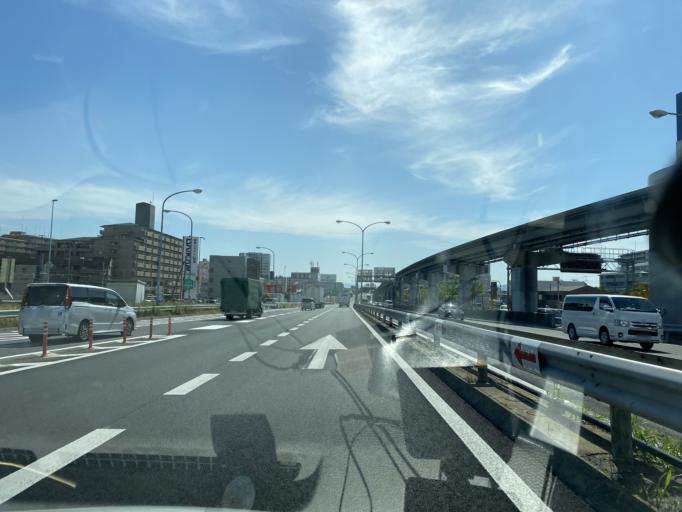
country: JP
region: Osaka
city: Ibaraki
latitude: 34.8082
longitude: 135.5477
